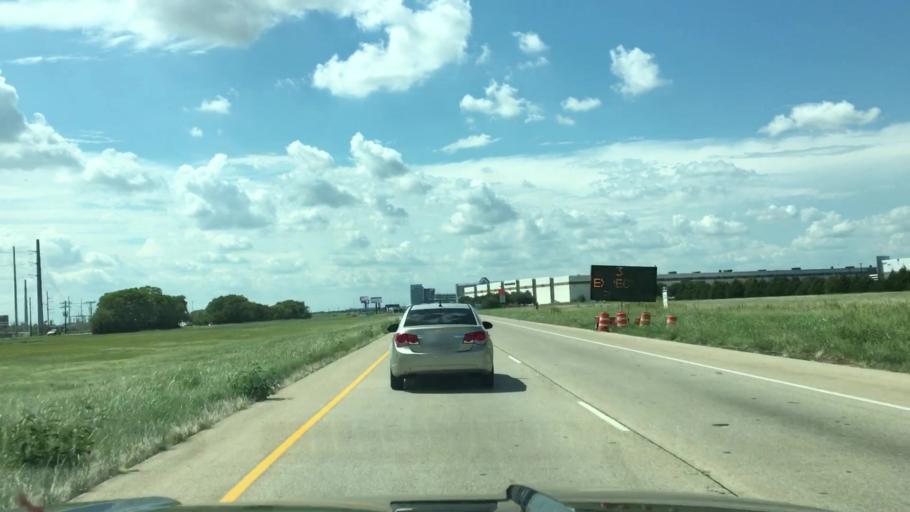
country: US
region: Texas
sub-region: Denton County
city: Roanoke
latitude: 33.0259
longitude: -97.2628
